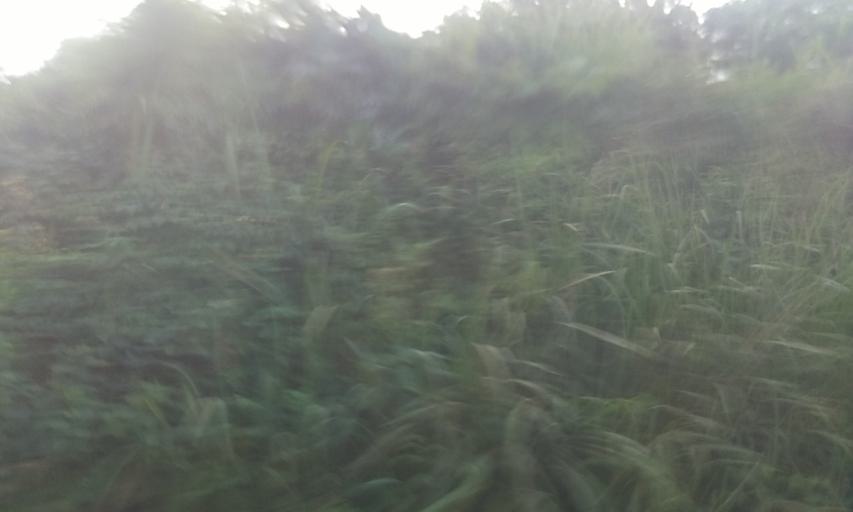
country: UG
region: Central Region
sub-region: Wakiso District
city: Kajansi
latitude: 0.2415
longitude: 32.4976
